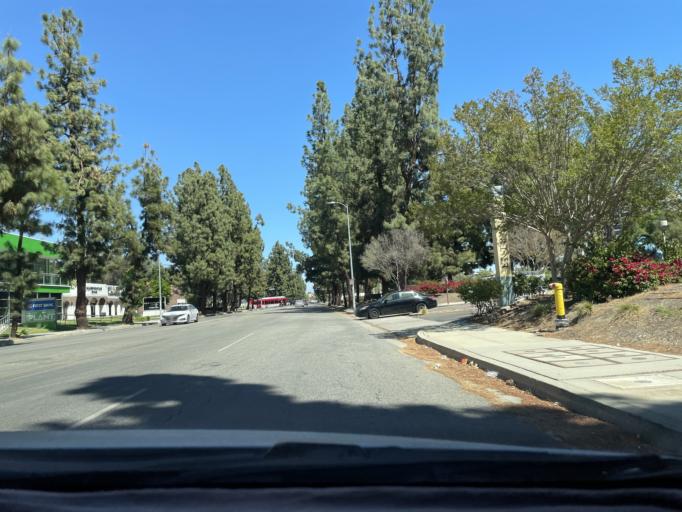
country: US
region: California
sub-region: Los Angeles County
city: Woodland Hills
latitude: 34.1828
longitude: -118.6036
